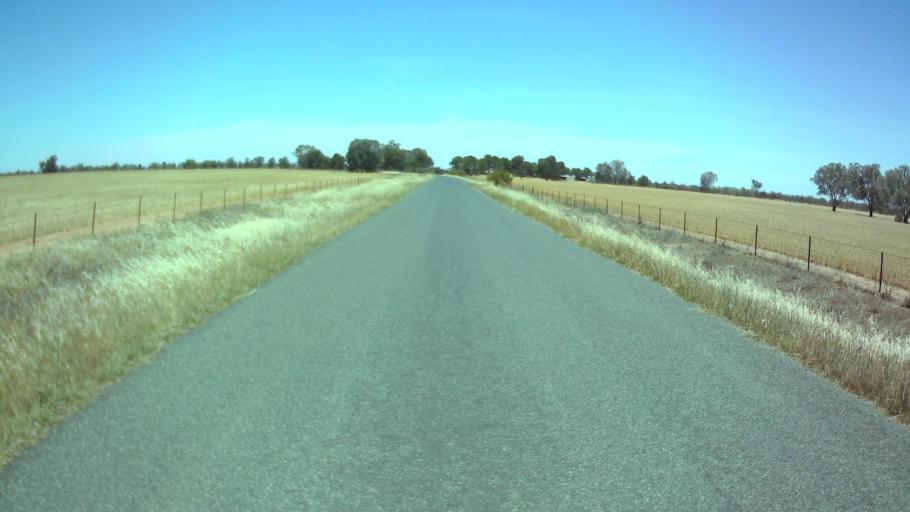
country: AU
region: New South Wales
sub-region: Weddin
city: Grenfell
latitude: -34.0433
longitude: 147.7862
